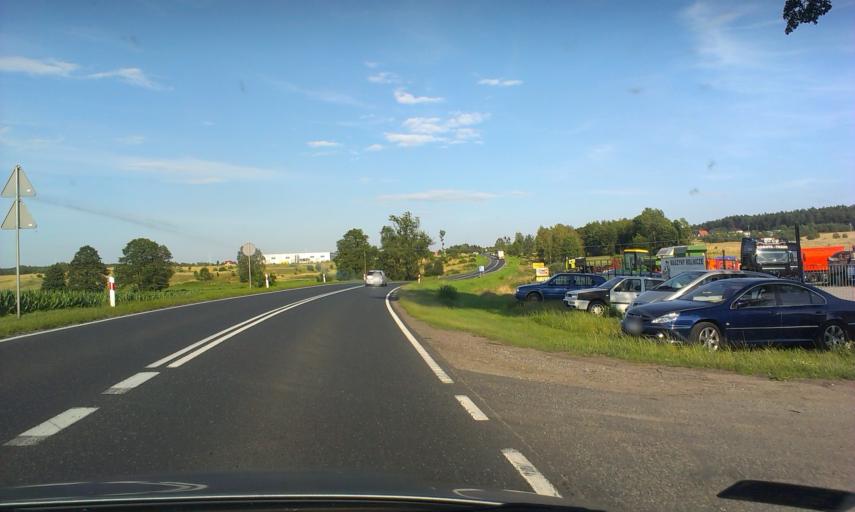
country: PL
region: Kujawsko-Pomorskie
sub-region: Powiat bydgoski
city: Sicienko
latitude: 53.1608
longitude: 17.8168
